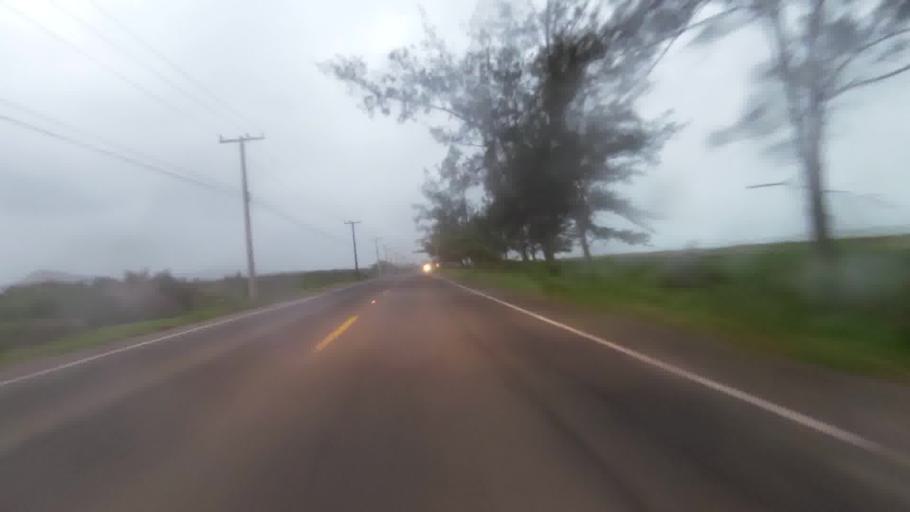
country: BR
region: Espirito Santo
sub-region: Itapemirim
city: Itapemirim
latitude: -20.9389
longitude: -40.8031
